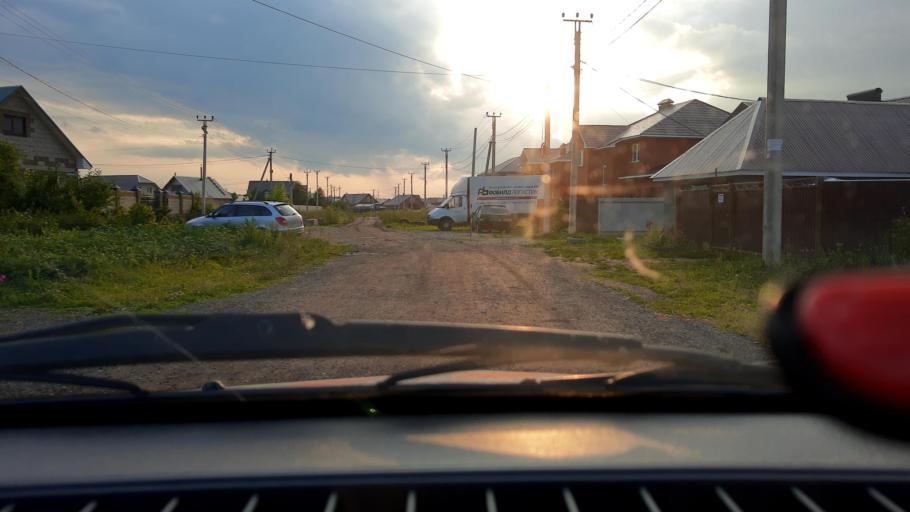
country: RU
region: Bashkortostan
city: Ufa
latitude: 54.6316
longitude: 55.9173
